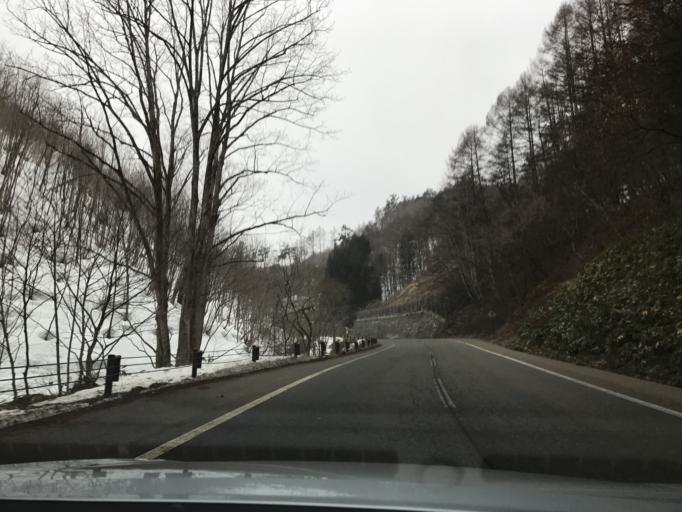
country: JP
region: Nagano
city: Omachi
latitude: 36.5822
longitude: 137.8831
